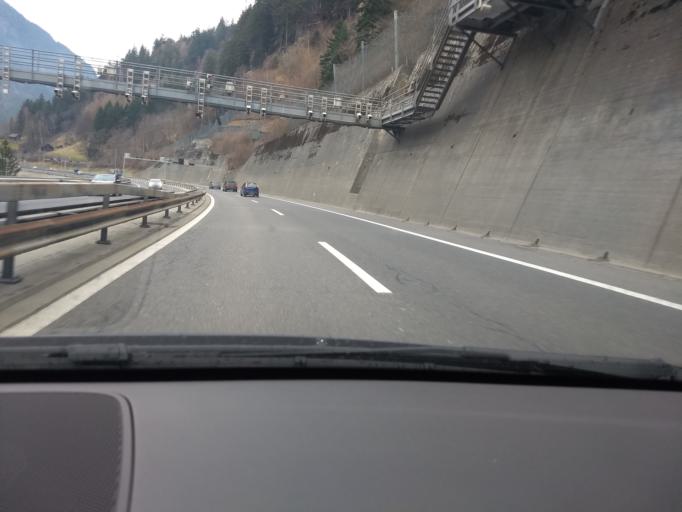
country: CH
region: Uri
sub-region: Uri
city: Silenen
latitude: 46.7443
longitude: 8.6436
